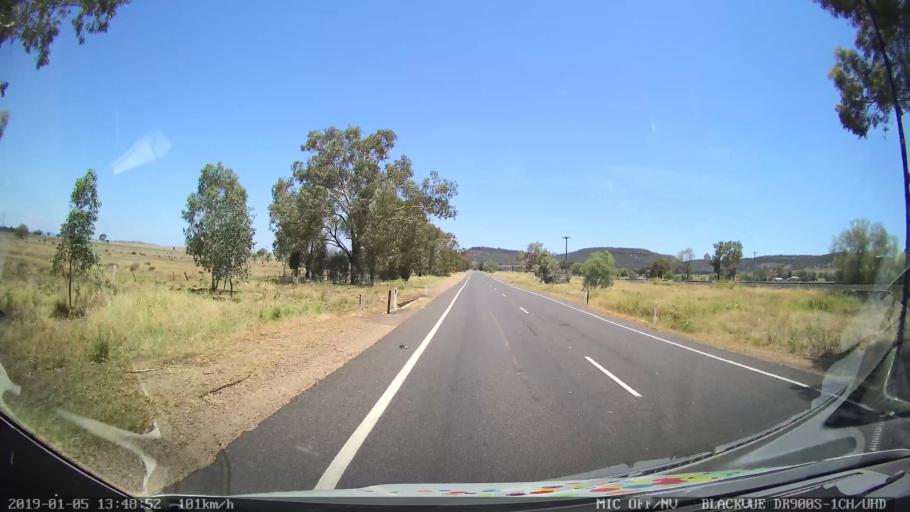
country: AU
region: New South Wales
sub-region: Gunnedah
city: Gunnedah
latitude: -31.0078
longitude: 150.2758
